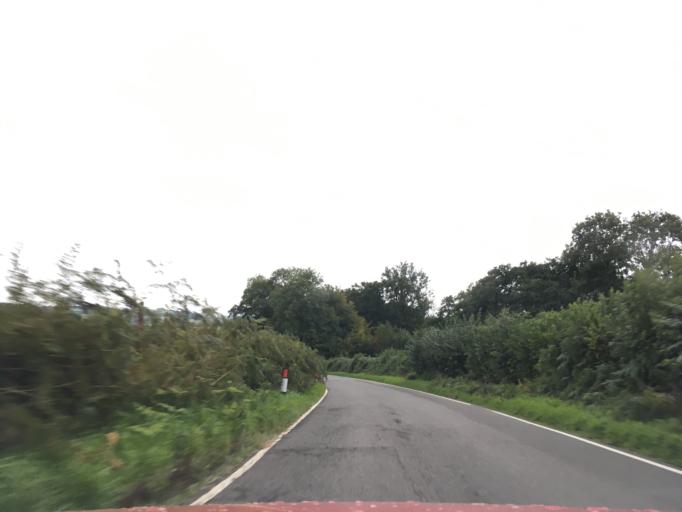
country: GB
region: Wales
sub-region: Monmouthshire
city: Llangwm
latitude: 51.6656
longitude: -2.8630
